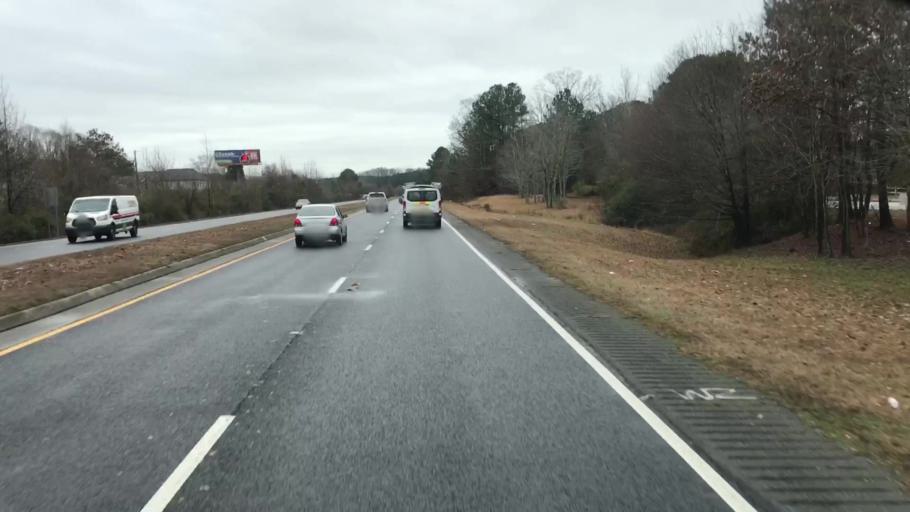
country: US
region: Georgia
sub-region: Gwinnett County
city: Snellville
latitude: 33.8810
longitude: -84.0284
